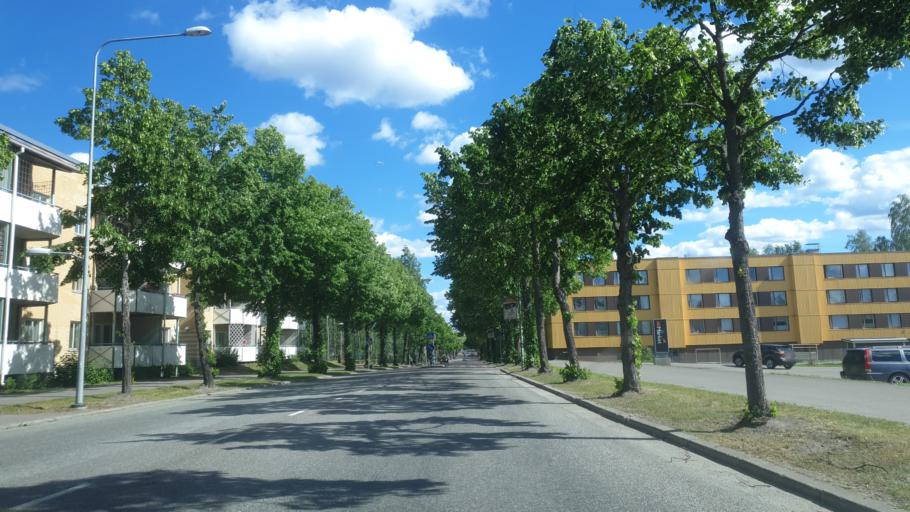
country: FI
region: Northern Savo
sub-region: Varkaus
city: Varkaus
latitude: 62.3275
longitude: 27.8909
